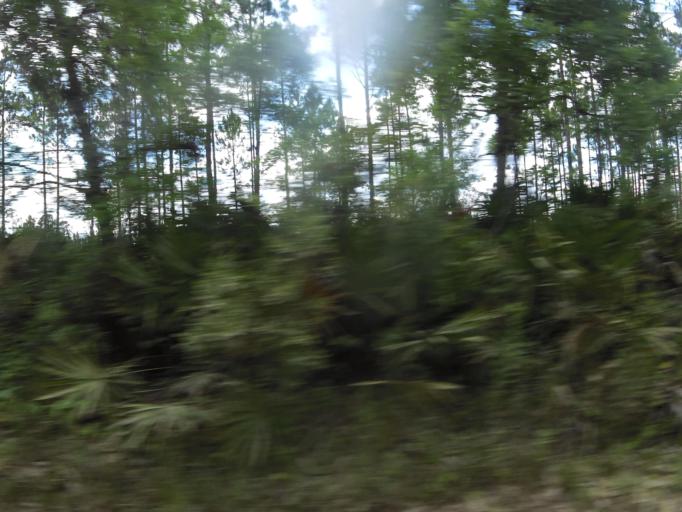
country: US
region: Florida
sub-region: Clay County
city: Asbury Lake
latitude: 29.8939
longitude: -81.8686
